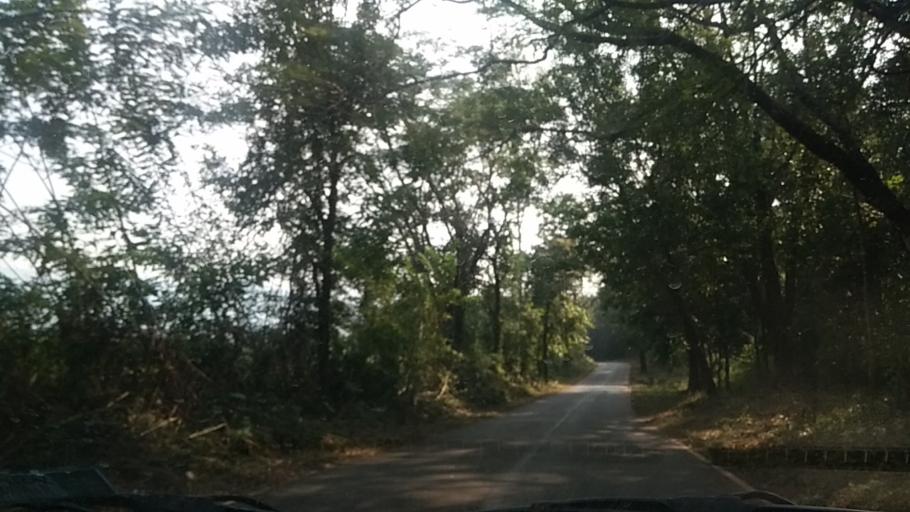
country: IN
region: Goa
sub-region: South Goa
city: Sanguem
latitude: 15.2125
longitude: 74.2066
